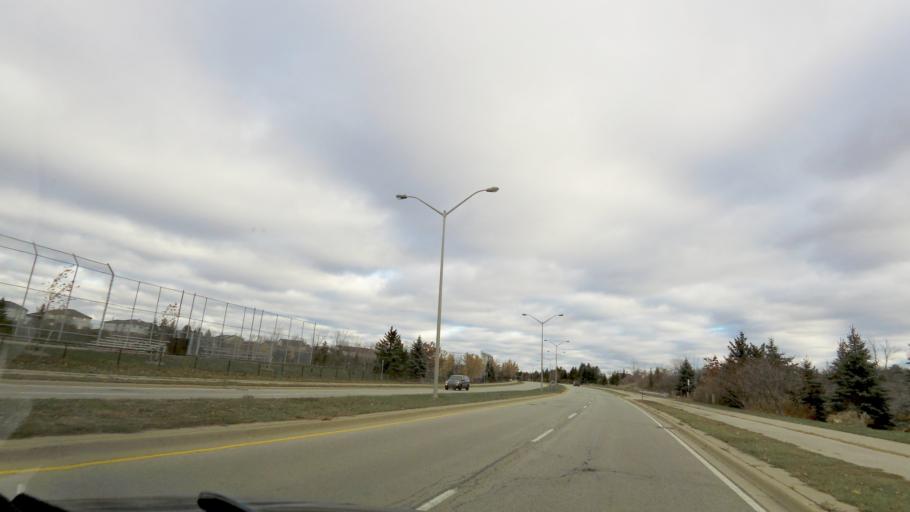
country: CA
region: Ontario
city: Oakville
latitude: 43.4603
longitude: -79.7362
